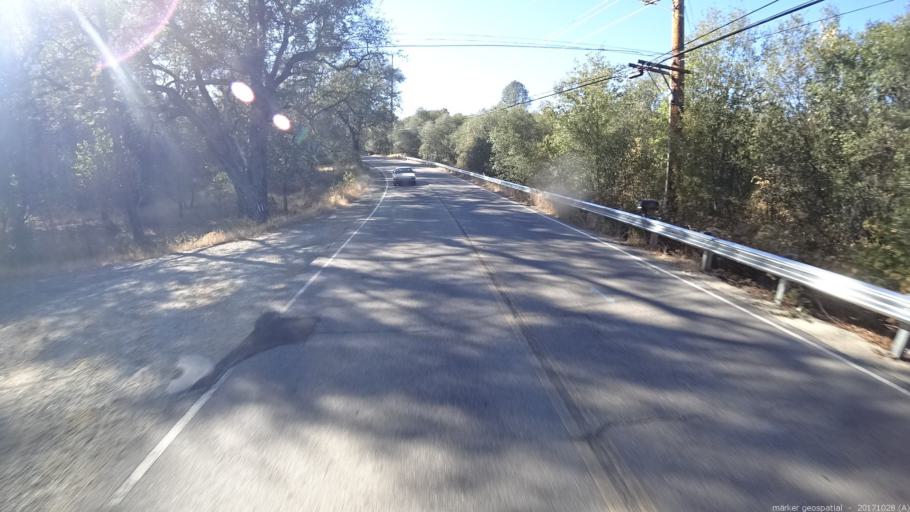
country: US
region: California
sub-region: Shasta County
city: Redding
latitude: 40.6260
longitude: -122.4145
